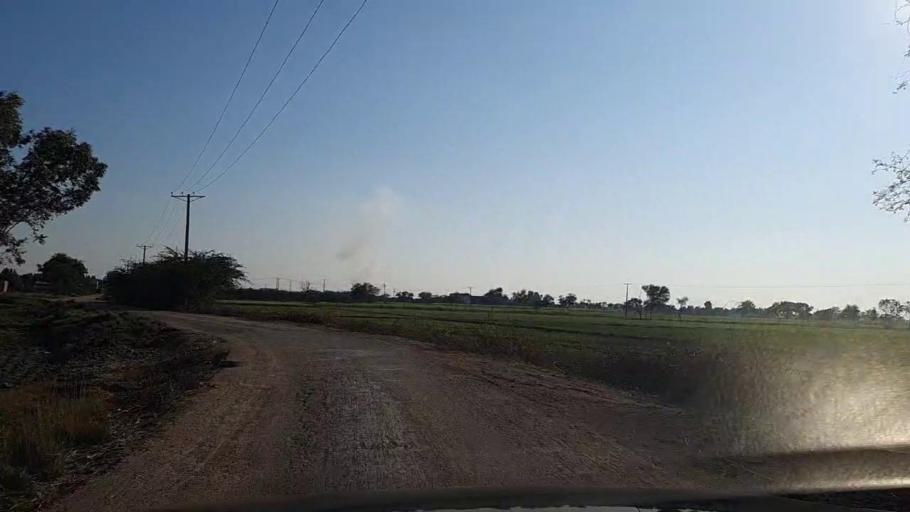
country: PK
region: Sindh
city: Nawabshah
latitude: 26.2068
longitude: 68.3749
